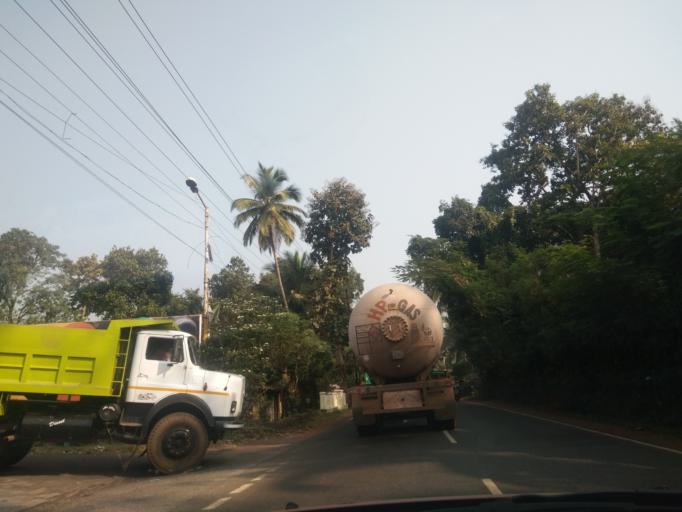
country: IN
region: Goa
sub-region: North Goa
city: Queula
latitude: 15.3705
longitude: 74.0098
